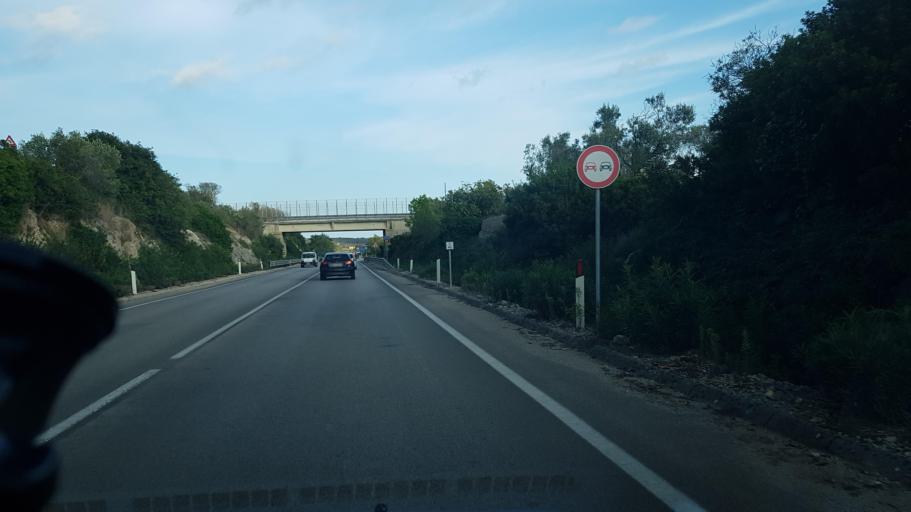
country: IT
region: Apulia
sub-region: Provincia di Lecce
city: Castrignano del Capo
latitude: 39.8188
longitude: 18.3520
